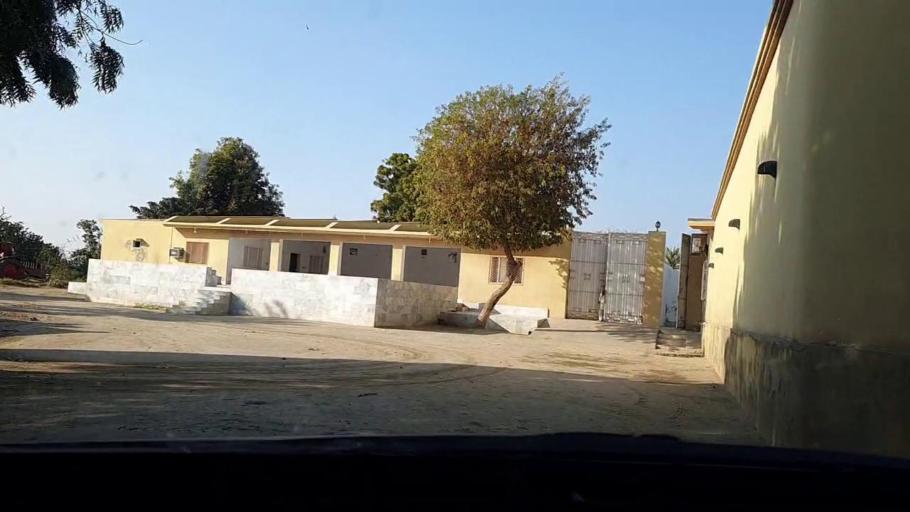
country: PK
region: Sindh
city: Tando Mittha Khan
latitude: 25.8582
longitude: 69.3332
